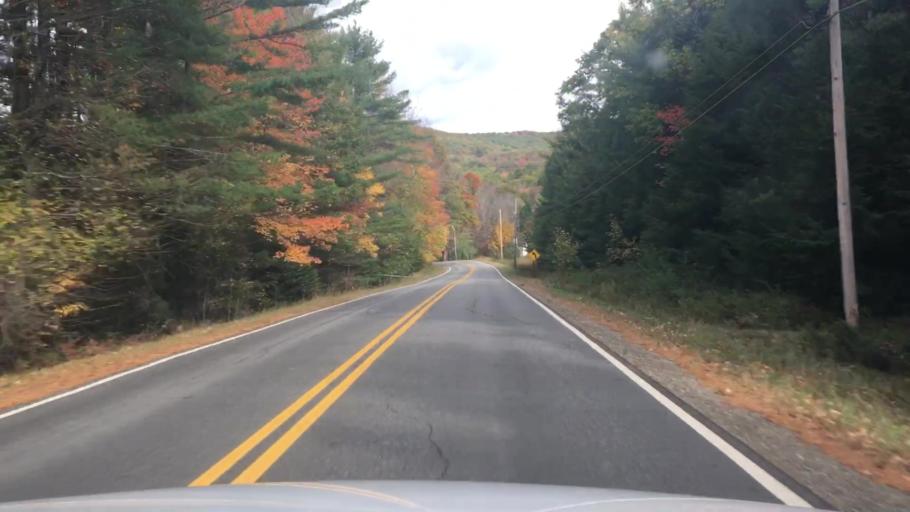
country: US
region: Maine
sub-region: Knox County
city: Hope
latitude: 44.3084
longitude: -69.1155
